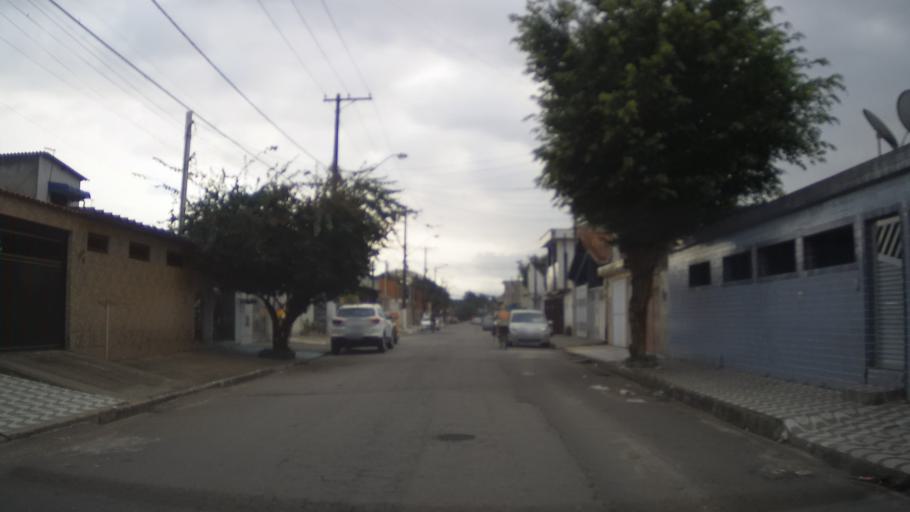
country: BR
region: Sao Paulo
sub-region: Praia Grande
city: Praia Grande
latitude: -24.0058
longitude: -46.4464
